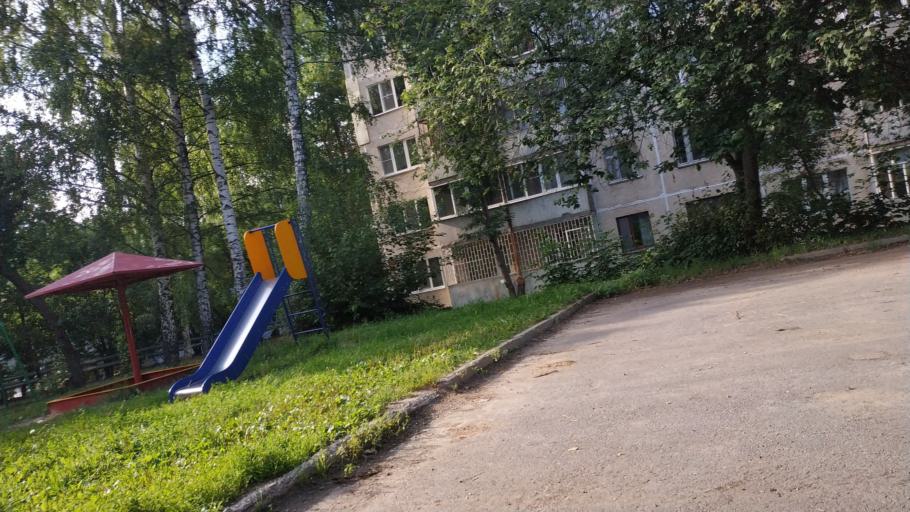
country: RU
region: Chuvashia
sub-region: Cheboksarskiy Rayon
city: Cheboksary
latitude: 56.1451
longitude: 47.1826
